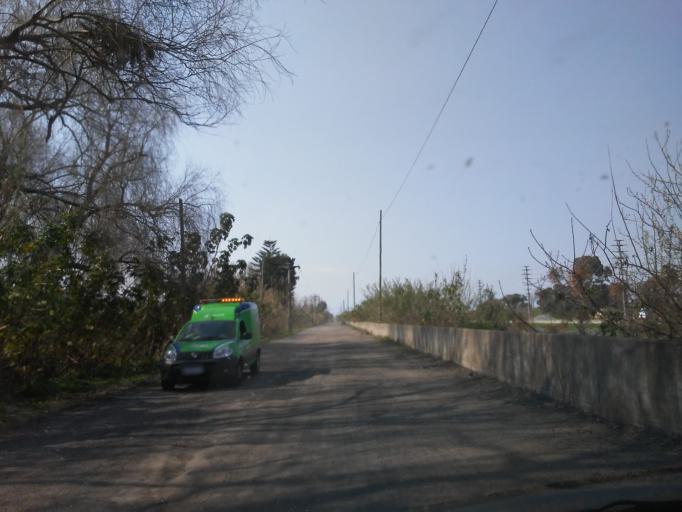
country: AR
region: Buenos Aires
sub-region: Partido de Avellaneda
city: Avellaneda
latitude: -34.6808
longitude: -58.3158
